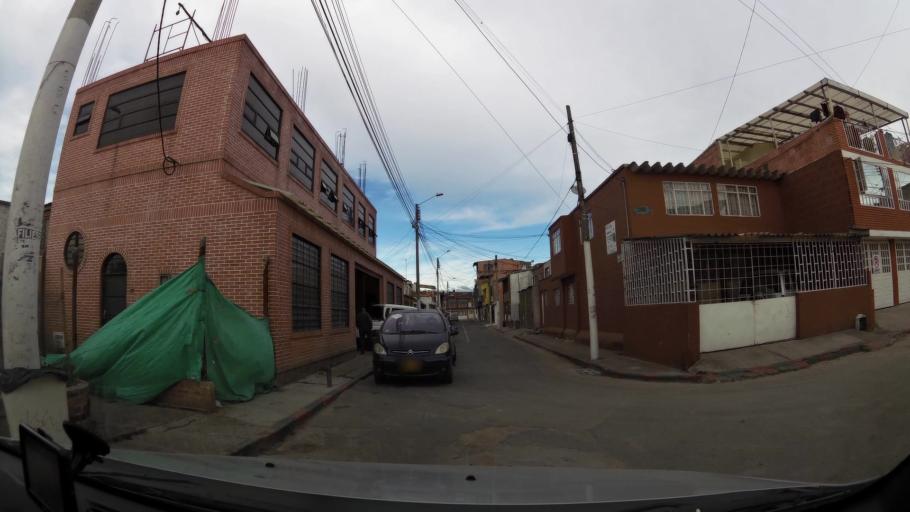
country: CO
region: Cundinamarca
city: Soacha
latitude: 4.6165
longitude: -74.1616
